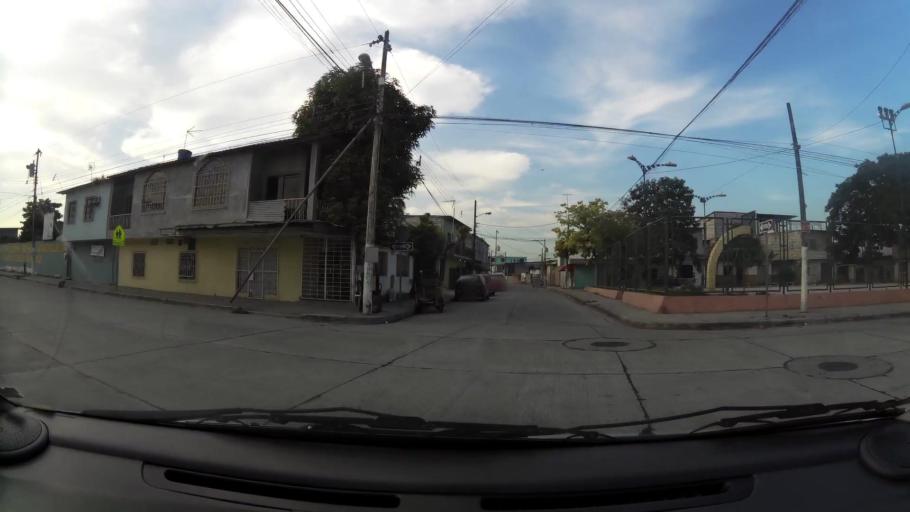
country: EC
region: Guayas
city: Eloy Alfaro
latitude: -2.0917
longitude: -79.9079
